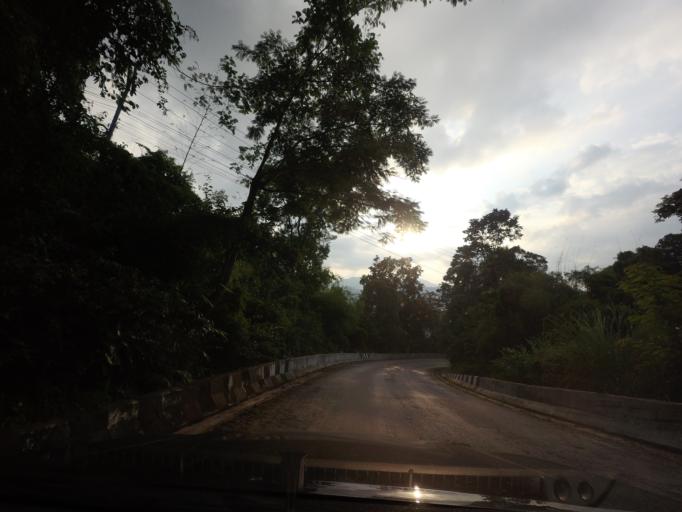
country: TH
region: Loei
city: Na Haeo
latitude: 17.3627
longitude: 101.0519
